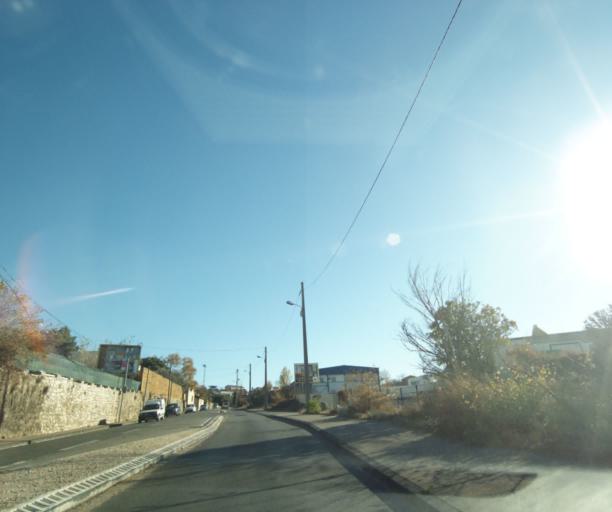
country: FR
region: Provence-Alpes-Cote d'Azur
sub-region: Departement des Bouches-du-Rhone
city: Marseille 15
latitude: 43.3536
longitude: 5.3528
